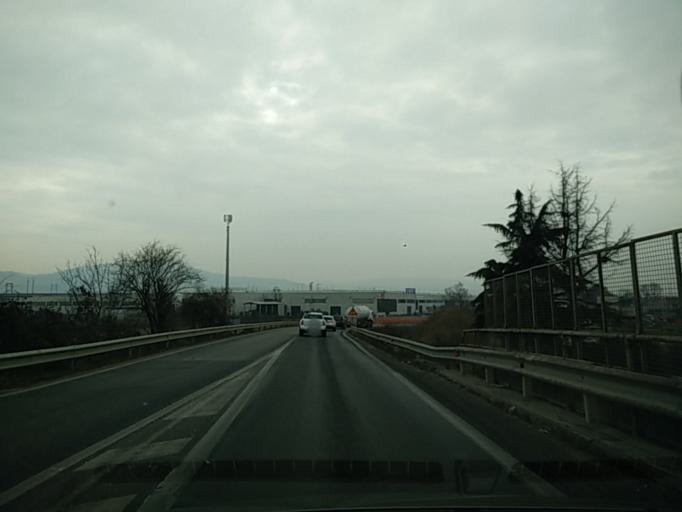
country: IT
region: Piedmont
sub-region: Provincia di Torino
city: Settimo Torinese
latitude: 45.1358
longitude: 7.7364
